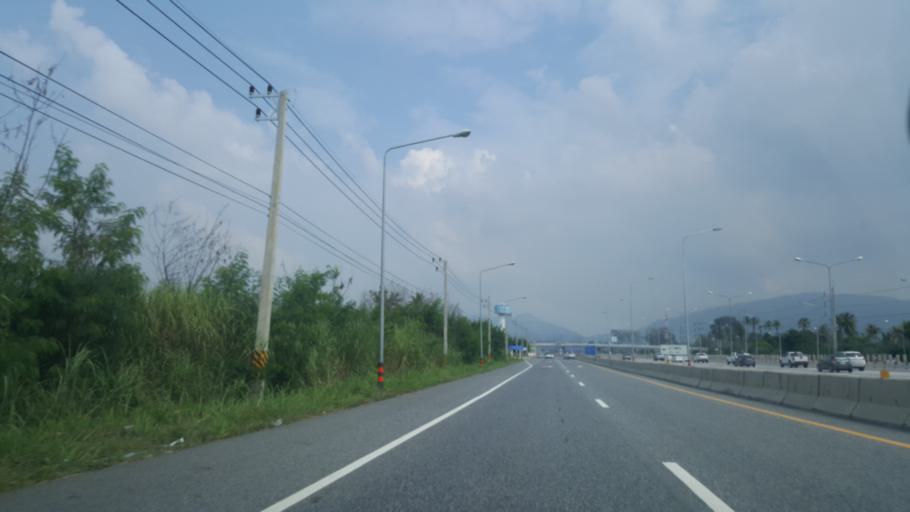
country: TH
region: Chon Buri
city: Si Racha
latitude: 13.2052
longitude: 101.0031
